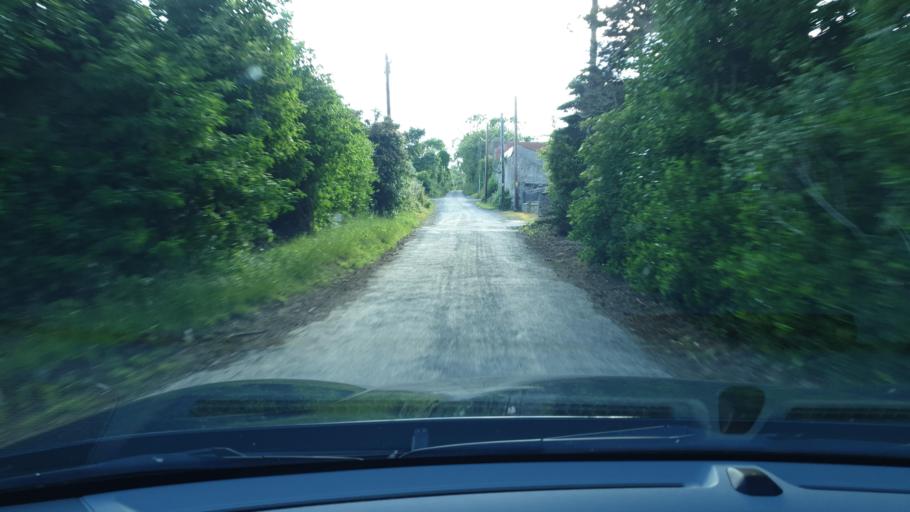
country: IE
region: Leinster
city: An Ros
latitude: 53.5508
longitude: -6.0917
